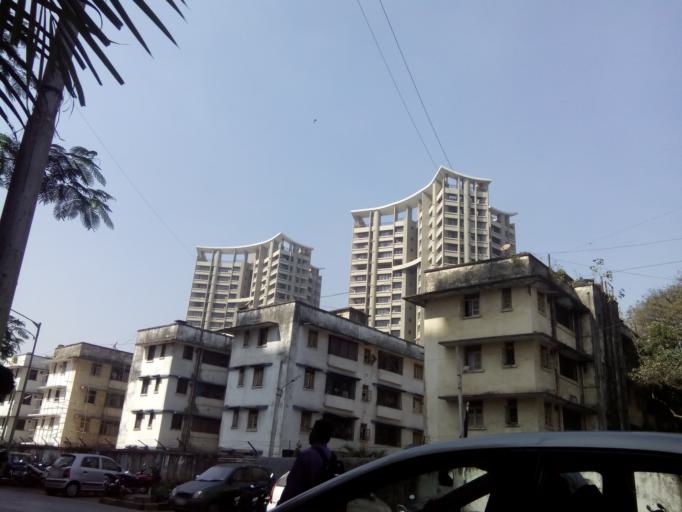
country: IN
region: Maharashtra
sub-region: Mumbai Suburban
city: Mumbai
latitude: 19.0511
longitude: 72.8580
